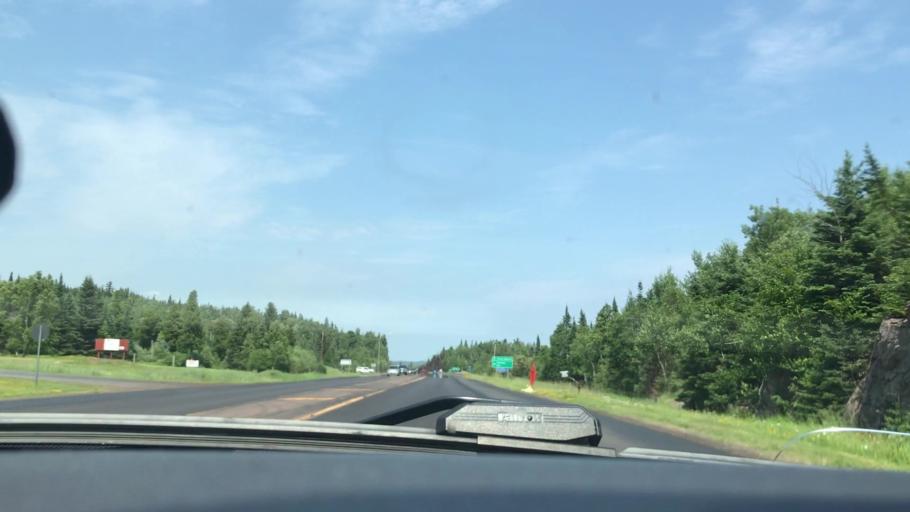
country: US
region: Minnesota
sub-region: Lake County
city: Silver Bay
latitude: 47.3448
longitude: -91.1896
